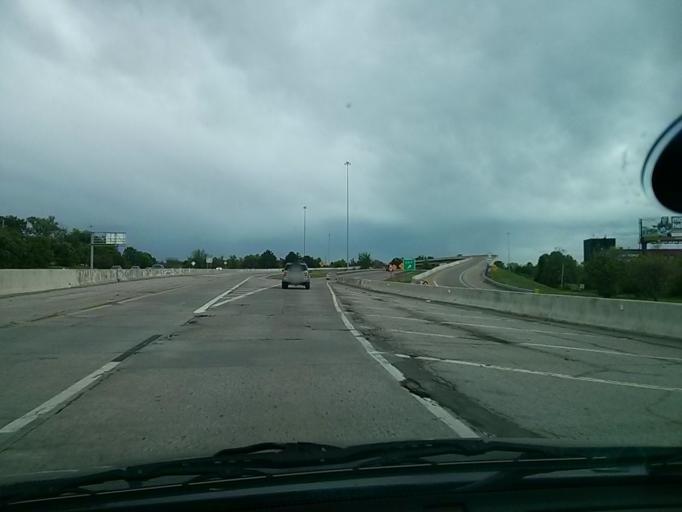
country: US
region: Oklahoma
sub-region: Tulsa County
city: Tulsa
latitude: 36.1472
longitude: -95.9799
